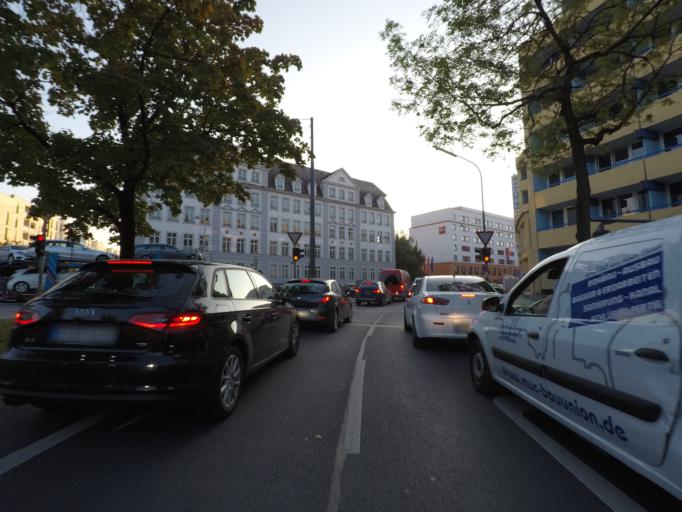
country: DE
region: Bavaria
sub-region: Upper Bavaria
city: Munich
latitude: 48.1455
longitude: 11.5415
